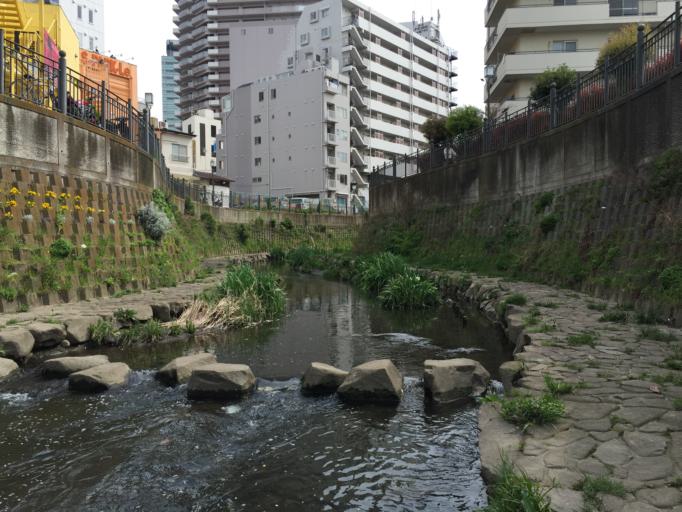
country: JP
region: Kanagawa
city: Yokohama
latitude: 35.4106
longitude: 139.5952
